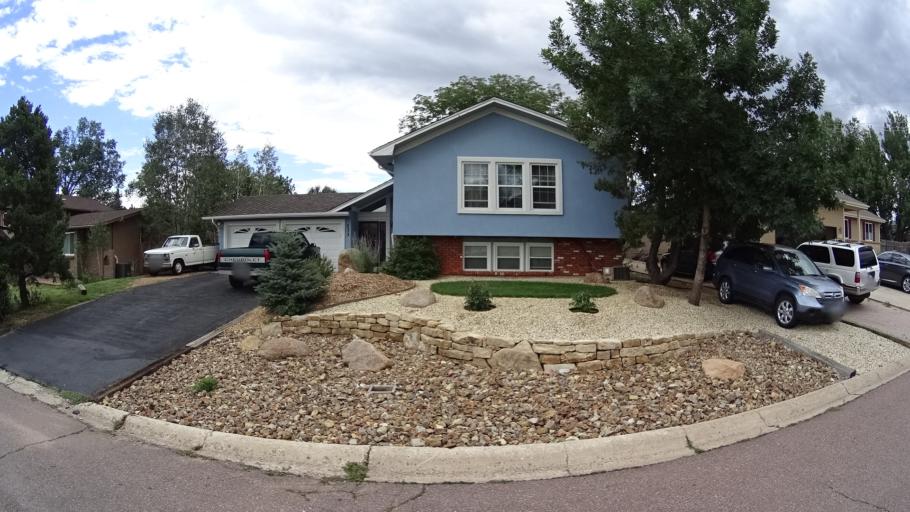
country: US
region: Colorado
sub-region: El Paso County
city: Manitou Springs
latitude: 38.8539
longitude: -104.8901
